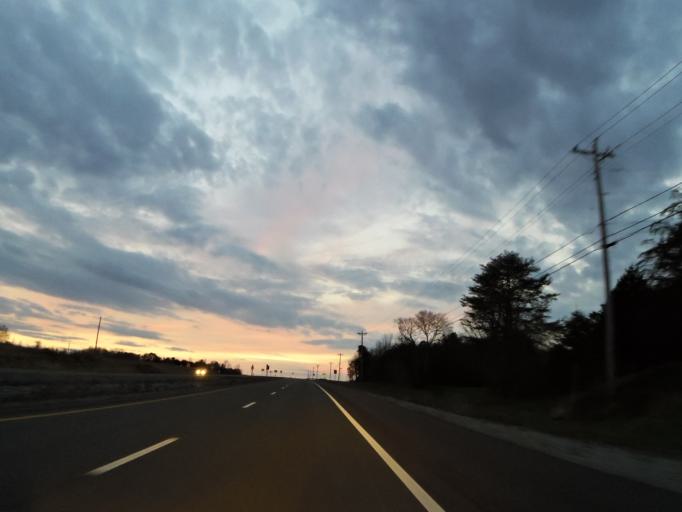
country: US
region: Tennessee
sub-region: Polk County
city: Benton
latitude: 35.2029
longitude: -84.6168
